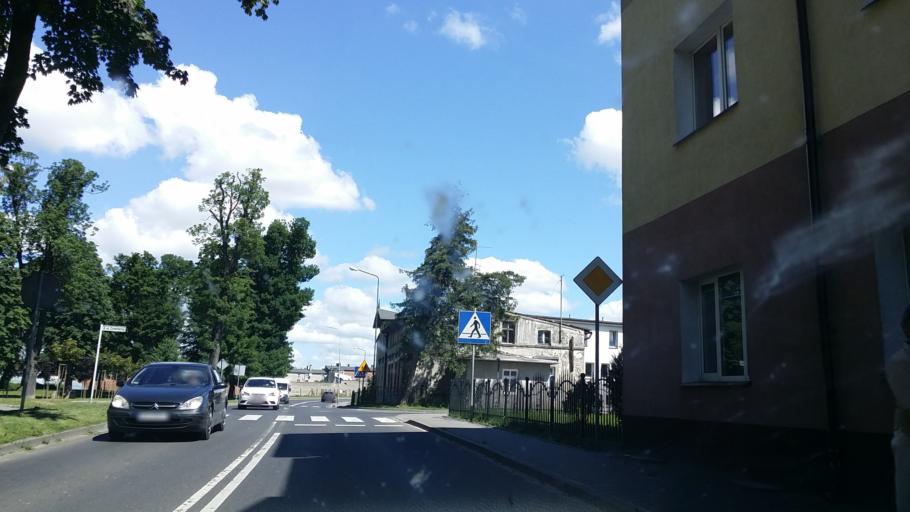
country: PL
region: West Pomeranian Voivodeship
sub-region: Powiat swidwinski
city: Swidwin
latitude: 53.7761
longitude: 15.7772
